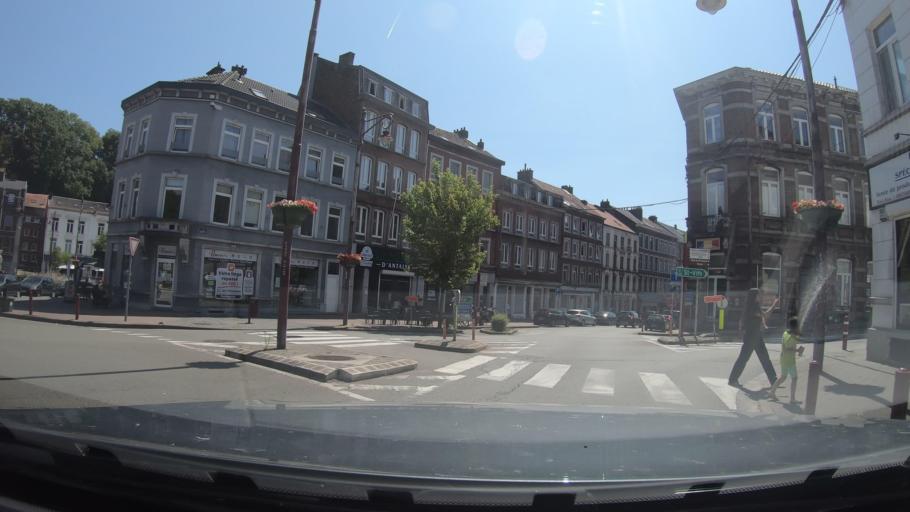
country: BE
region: Wallonia
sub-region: Province de Liege
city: Dison
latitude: 50.6098
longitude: 5.8541
